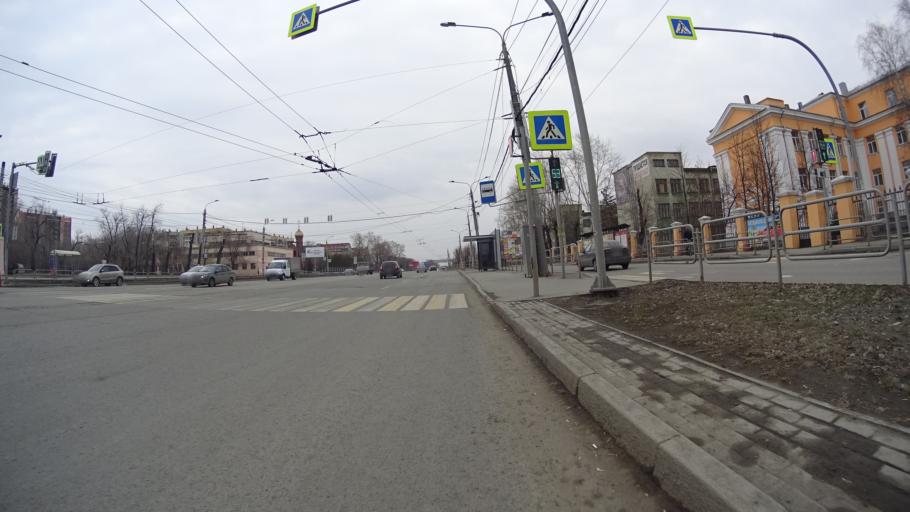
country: RU
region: Chelyabinsk
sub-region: Gorod Chelyabinsk
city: Chelyabinsk
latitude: 55.1600
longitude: 61.4520
